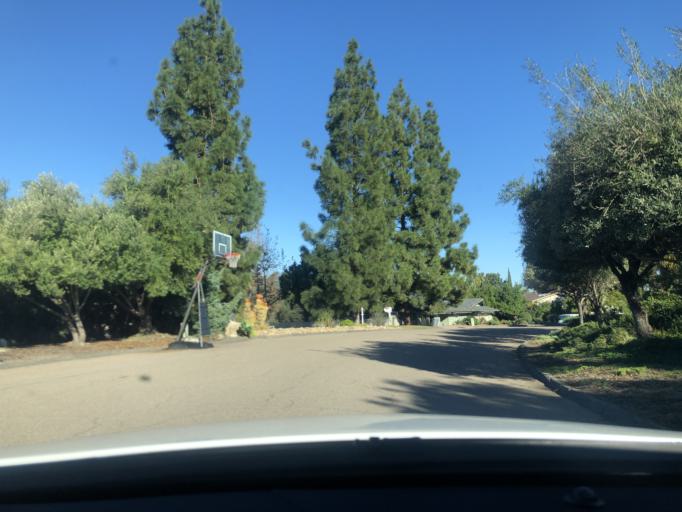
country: US
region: California
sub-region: San Diego County
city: Casa de Oro-Mount Helix
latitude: 32.7673
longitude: -116.9473
